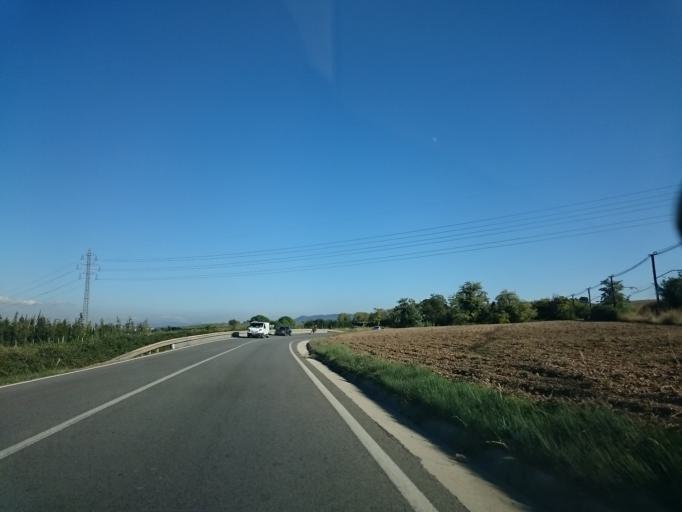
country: ES
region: Catalonia
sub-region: Provincia de Barcelona
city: Piera
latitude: 41.5146
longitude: 1.7672
